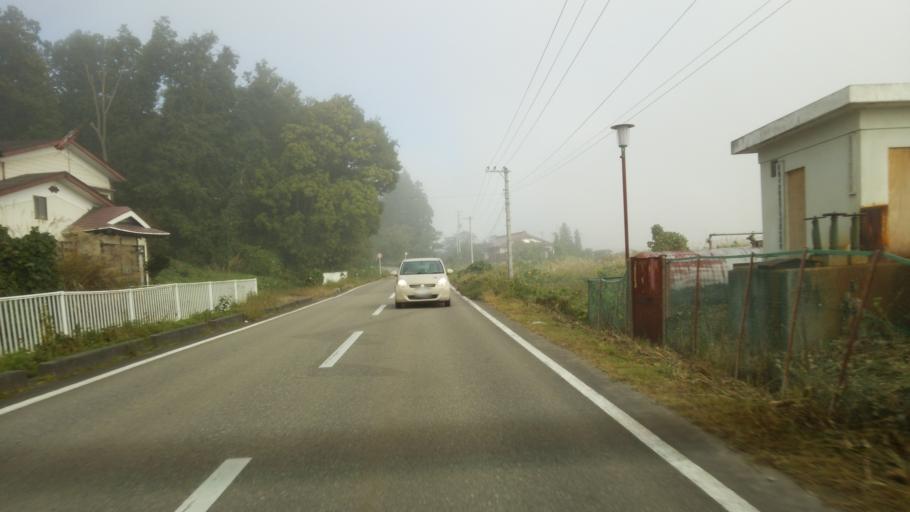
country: JP
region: Fukushima
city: Kitakata
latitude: 37.5128
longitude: 139.8220
